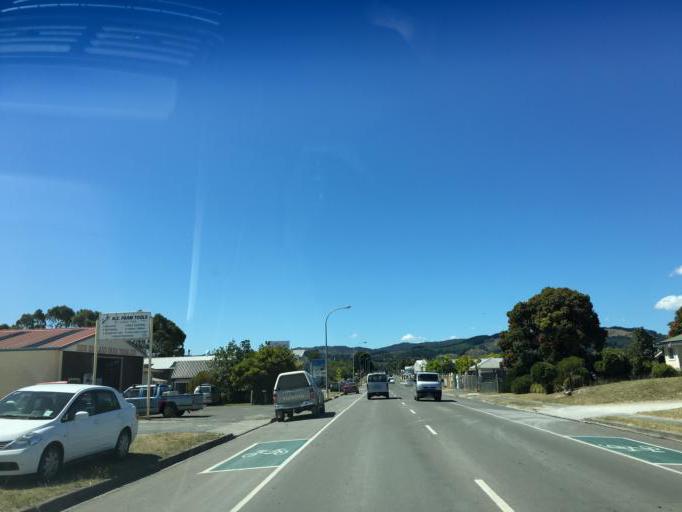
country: NZ
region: Gisborne
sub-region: Gisborne District
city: Gisborne
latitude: -38.6668
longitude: 178.0049
